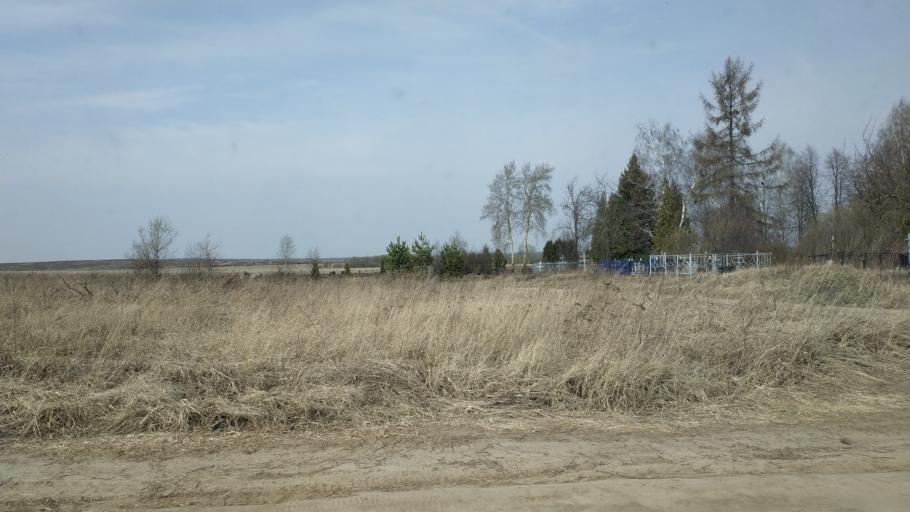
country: RU
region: Moskovskaya
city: Troitskoye
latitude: 55.3555
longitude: 38.4849
